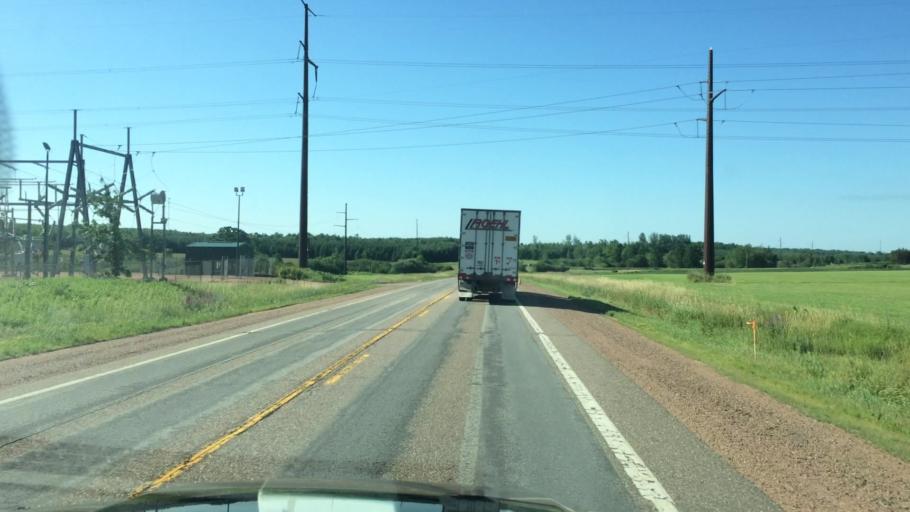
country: US
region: Wisconsin
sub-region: Marathon County
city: Athens
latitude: 44.9353
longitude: -90.0790
